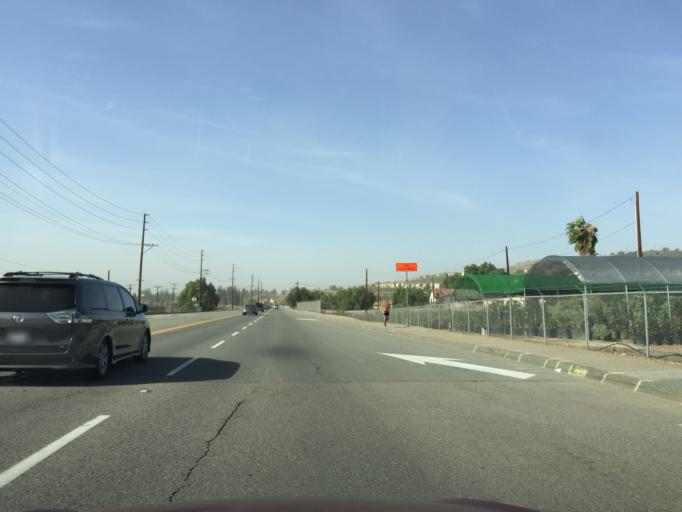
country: US
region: California
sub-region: Orange County
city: Yorba Linda
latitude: 33.9242
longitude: -117.8486
